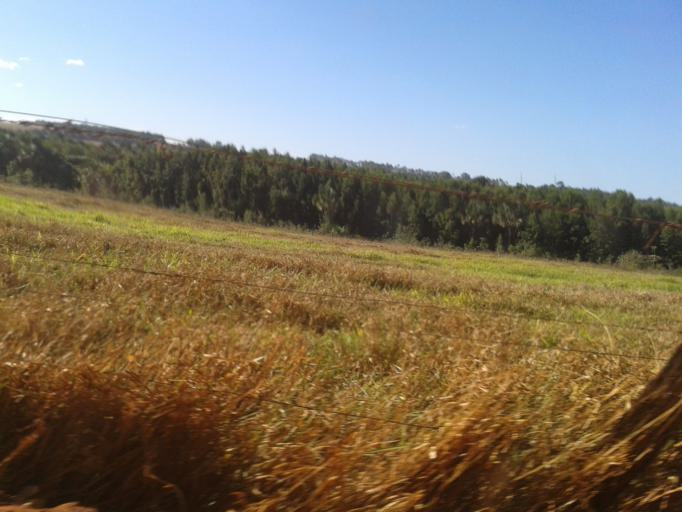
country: BR
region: Minas Gerais
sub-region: Centralina
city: Centralina
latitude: -18.7382
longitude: -49.1701
